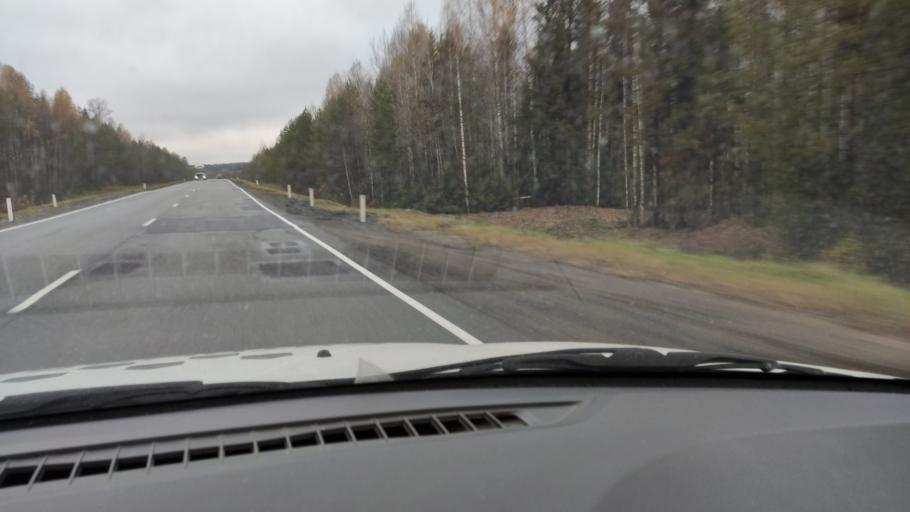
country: RU
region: Kirov
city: Dubrovka
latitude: 58.9036
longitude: 51.2793
